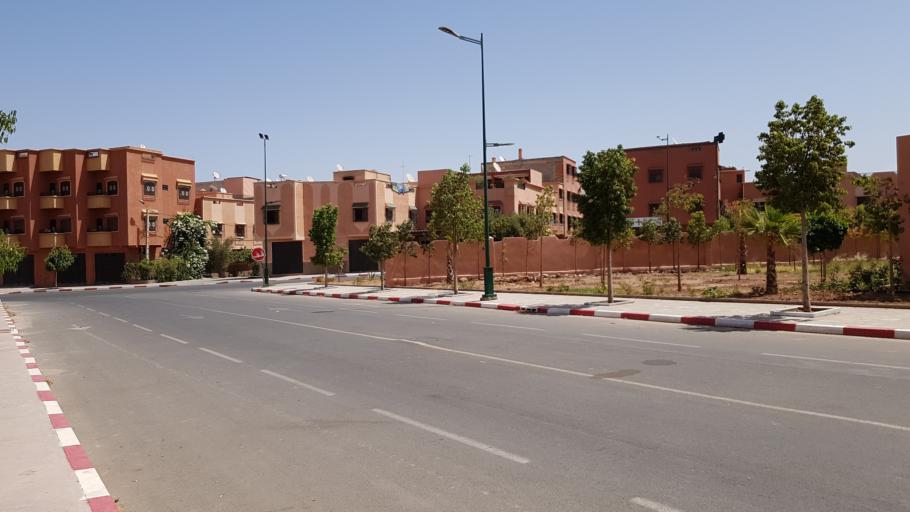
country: MA
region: Marrakech-Tensift-Al Haouz
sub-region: Marrakech
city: Marrakesh
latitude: 31.5916
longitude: -8.0277
